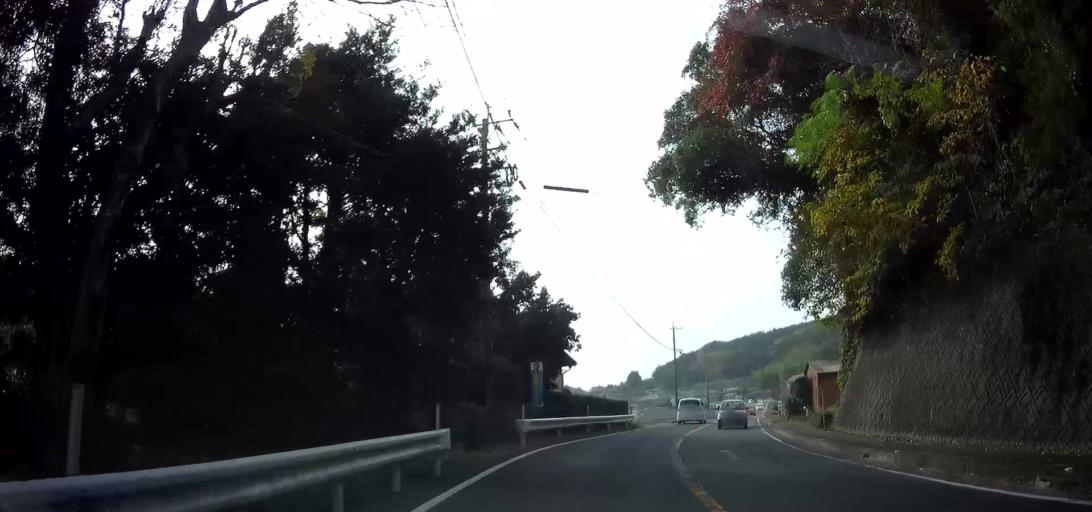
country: JP
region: Nagasaki
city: Shimabara
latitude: 32.7706
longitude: 130.2144
